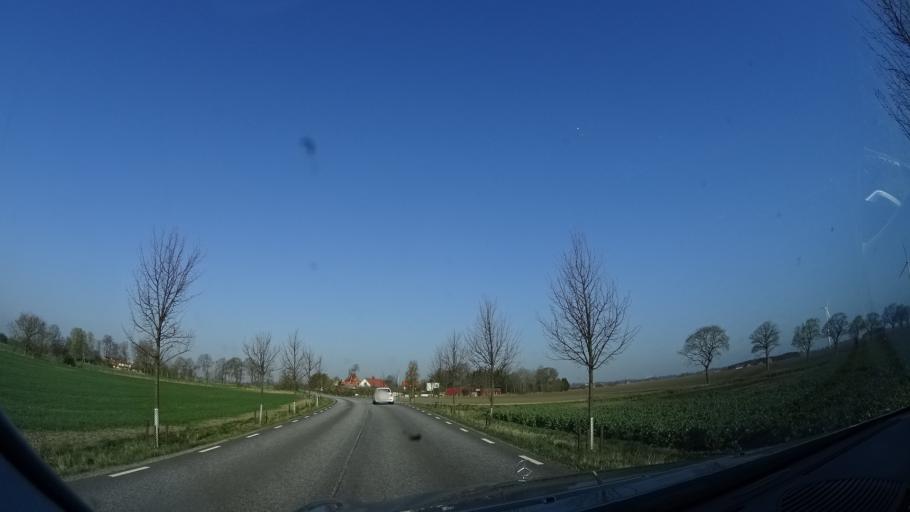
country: SE
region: Skane
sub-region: Eslovs Kommun
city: Eslov
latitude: 55.8075
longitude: 13.3519
